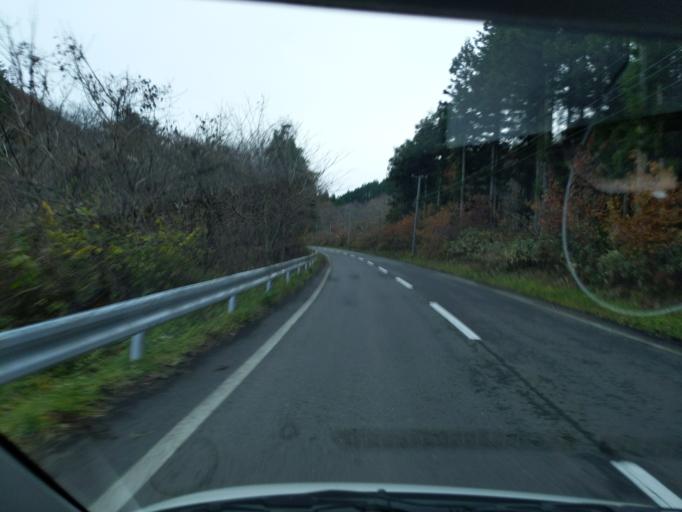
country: JP
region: Iwate
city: Tono
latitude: 39.1851
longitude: 141.3566
